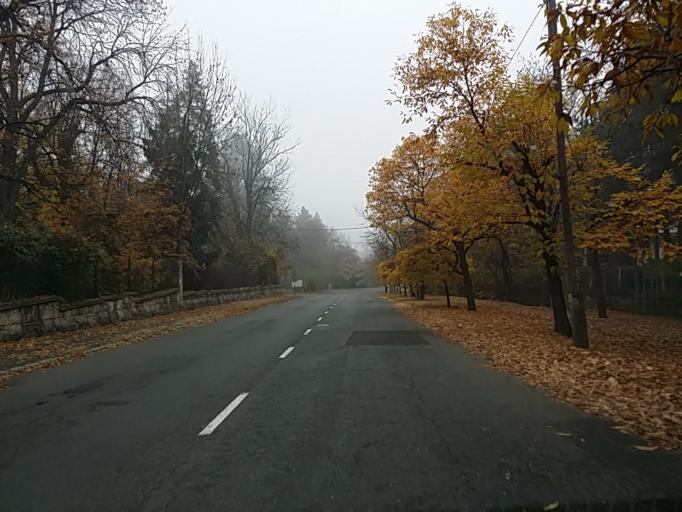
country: HU
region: Heves
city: Gyongyossolymos
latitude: 47.8330
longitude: 19.9680
